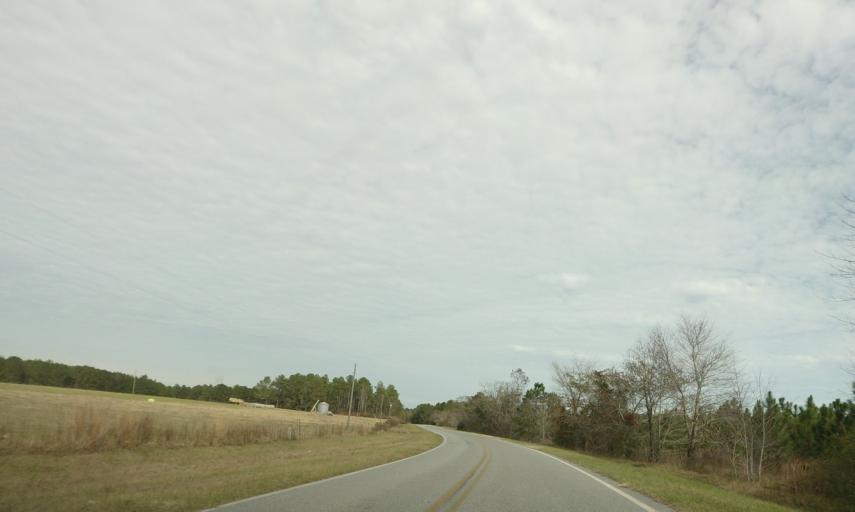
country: US
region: Georgia
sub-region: Dodge County
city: Chester
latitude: 32.4823
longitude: -83.0925
